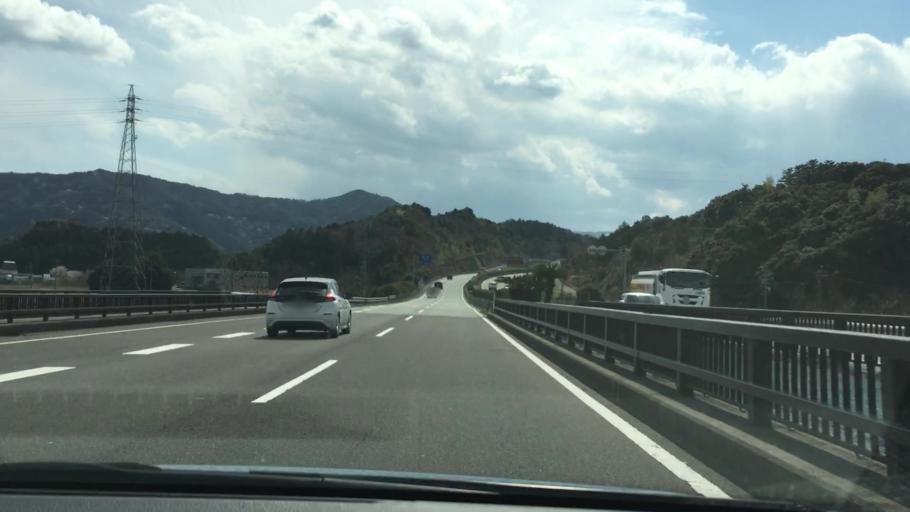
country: JP
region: Mie
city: Ise
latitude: 34.4841
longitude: 136.7533
